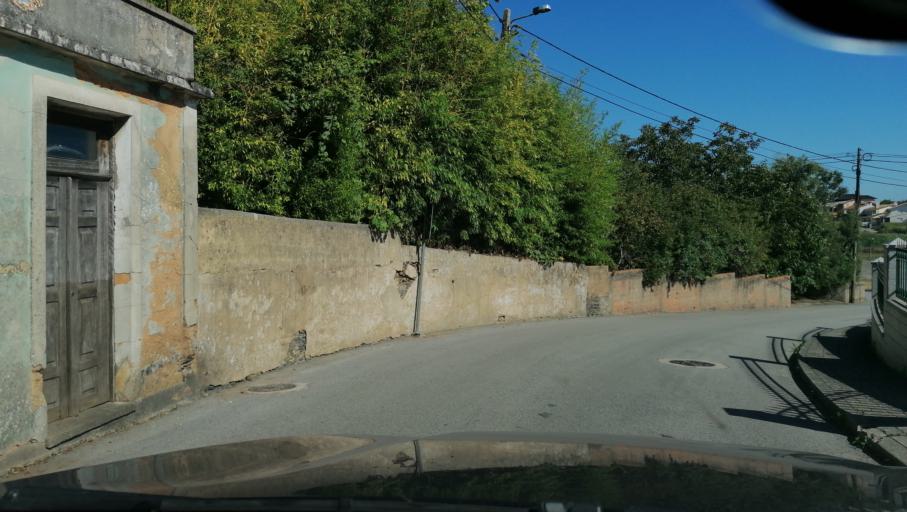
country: PT
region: Aveiro
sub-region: Estarreja
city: Salreu
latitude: 40.7503
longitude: -8.5556
